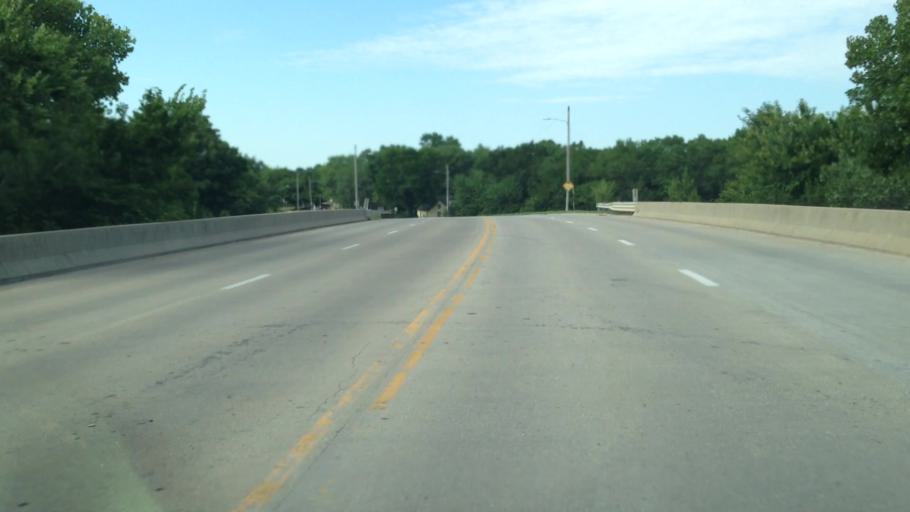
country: US
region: Kansas
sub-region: Labette County
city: Parsons
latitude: 37.3280
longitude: -95.2600
